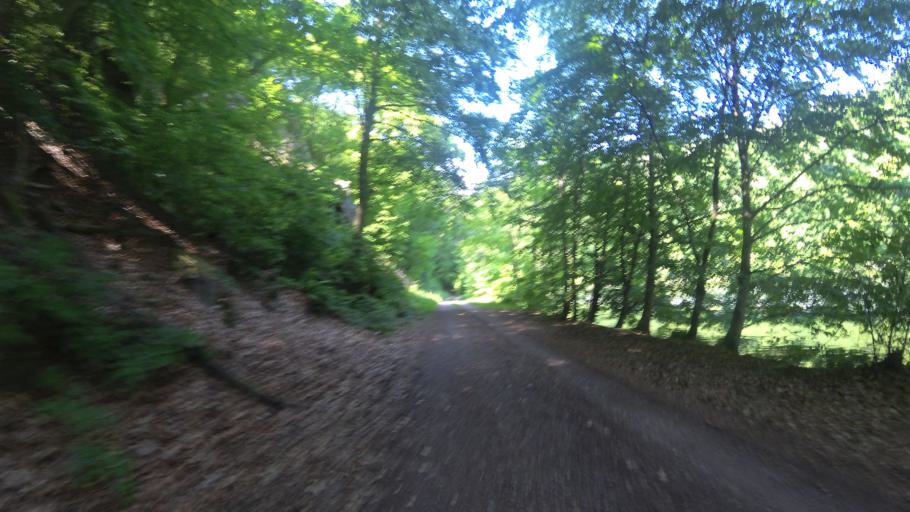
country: DE
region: Saarland
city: Mettlach
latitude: 49.4958
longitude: 6.5662
